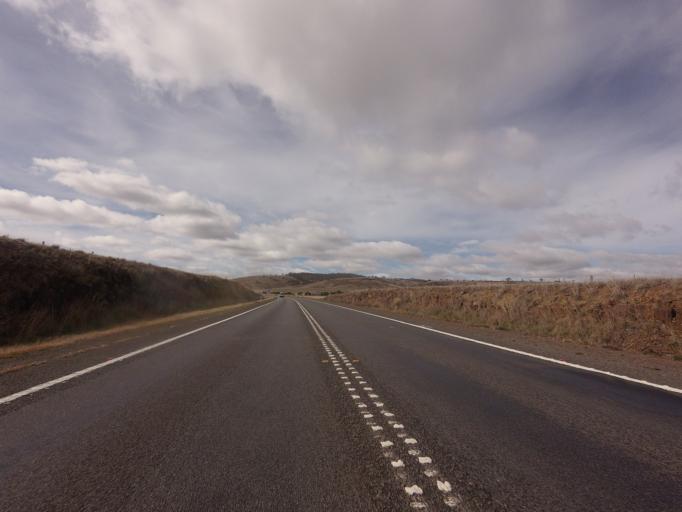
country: AU
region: Tasmania
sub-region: Brighton
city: Bridgewater
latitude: -42.3858
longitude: 147.3087
